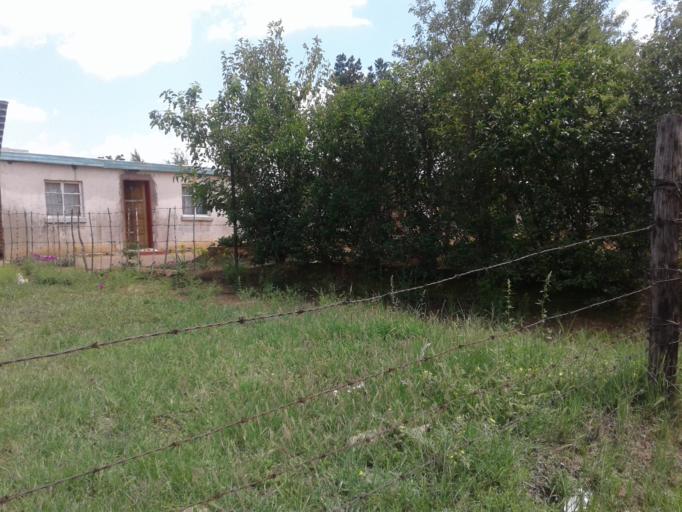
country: LS
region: Mafeteng
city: Mafeteng
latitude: -29.7599
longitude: 27.1119
